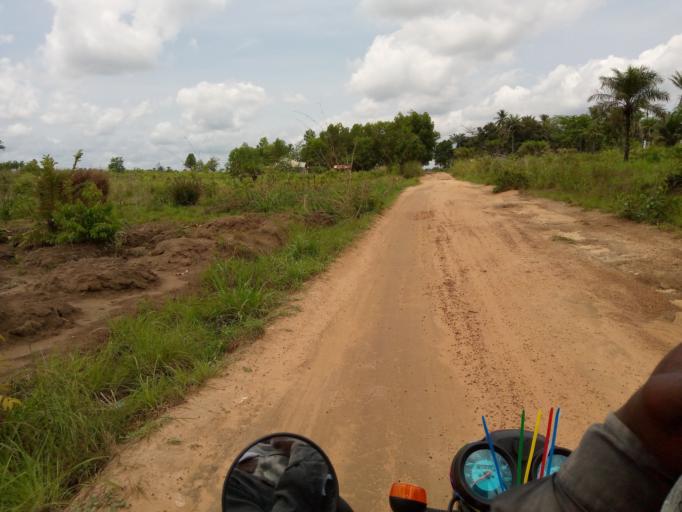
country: SL
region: Western Area
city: Waterloo
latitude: 8.3315
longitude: -12.9411
